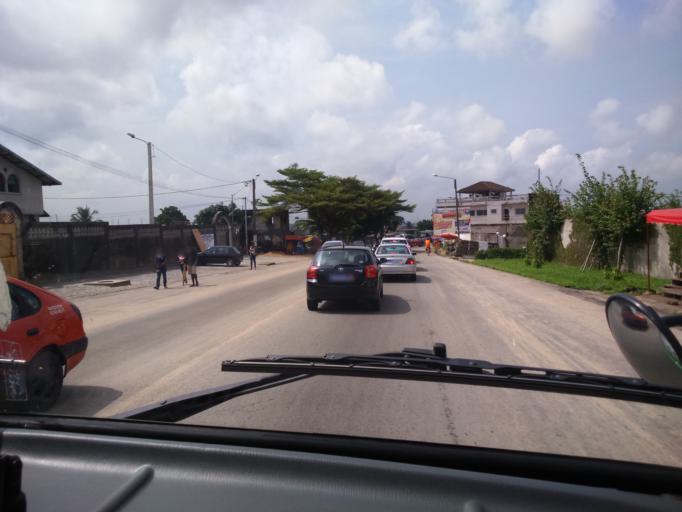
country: CI
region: Lagunes
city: Abobo
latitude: 5.3697
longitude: -3.9809
